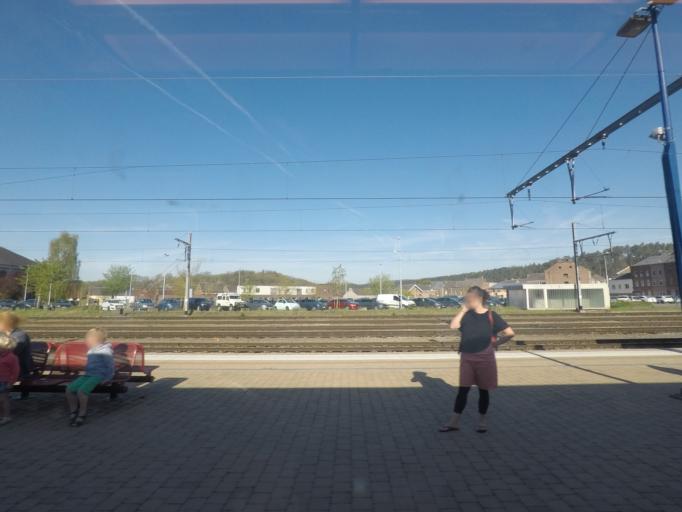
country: BE
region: Wallonia
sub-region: Province de Namur
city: Rochefort
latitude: 50.1601
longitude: 5.2663
